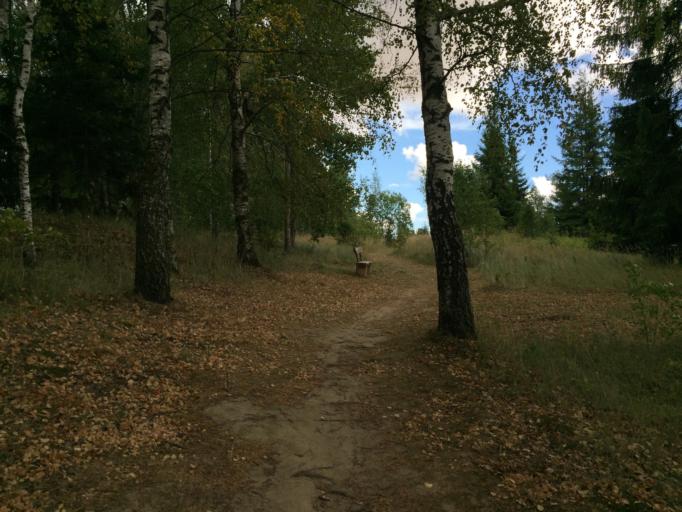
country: LT
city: Zagare
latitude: 56.3030
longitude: 23.3826
